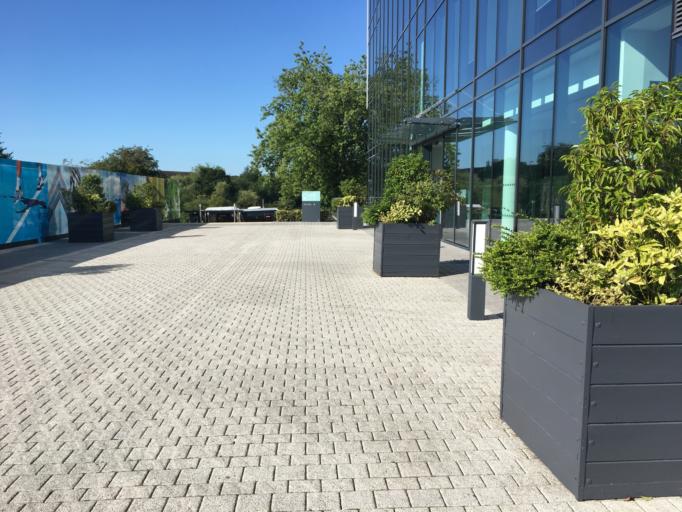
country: GB
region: England
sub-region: Bracknell Forest
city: Binfield
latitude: 51.4185
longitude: -0.7722
